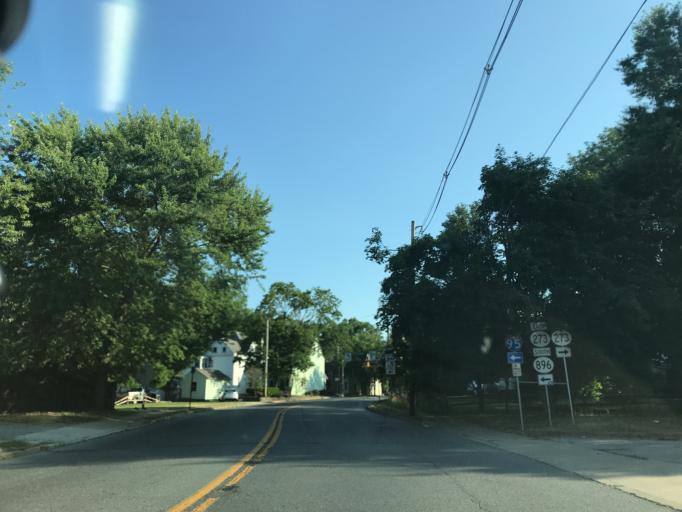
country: US
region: Delaware
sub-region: New Castle County
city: Newark
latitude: 39.6851
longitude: -75.7587
